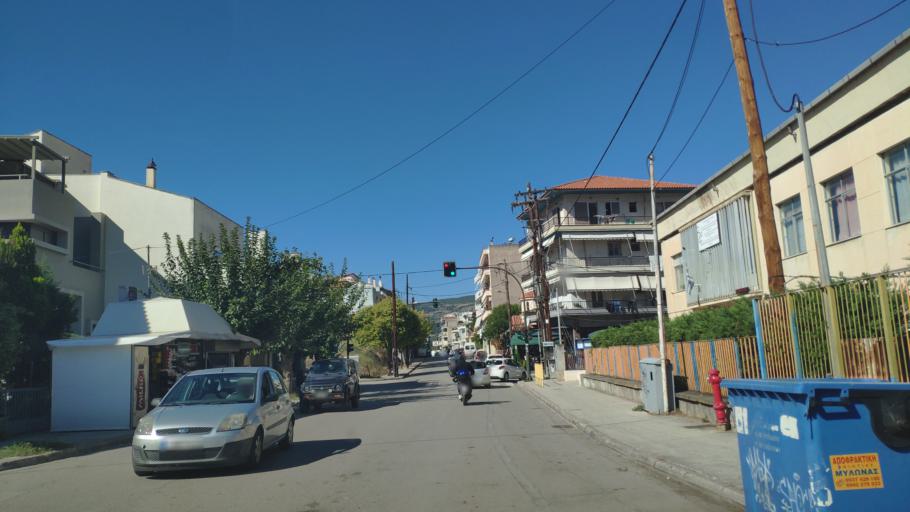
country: GR
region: Central Greece
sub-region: Nomos Voiotias
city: Livadeia
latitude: 38.4401
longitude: 22.8690
